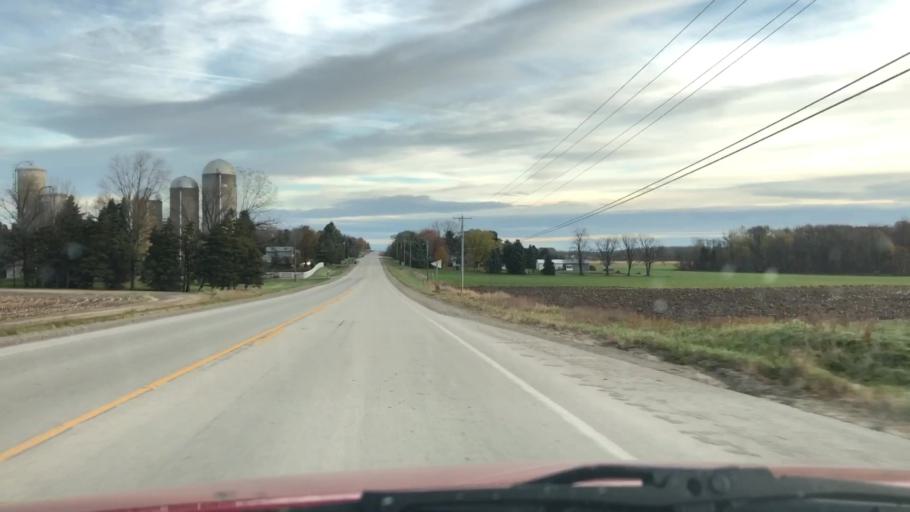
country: US
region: Wisconsin
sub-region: Brown County
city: Oneida
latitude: 44.4248
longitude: -88.2446
